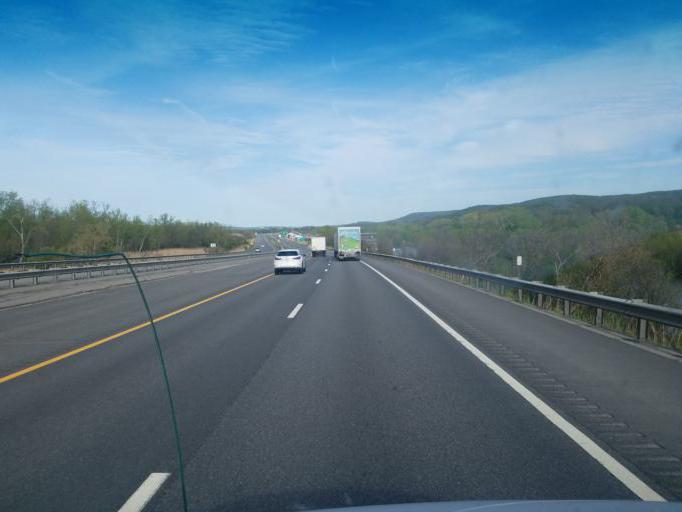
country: US
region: New York
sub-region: Herkimer County
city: Mohawk
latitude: 43.0173
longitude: -75.0067
